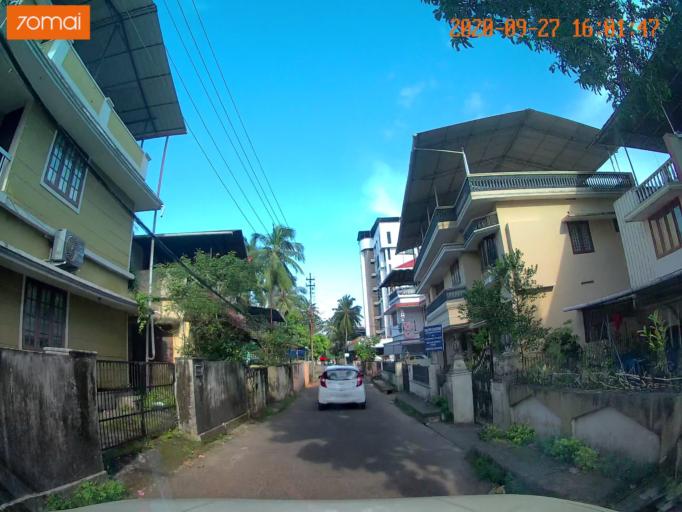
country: IN
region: Kerala
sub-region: Thrissur District
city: Trichur
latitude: 10.5197
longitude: 76.2034
